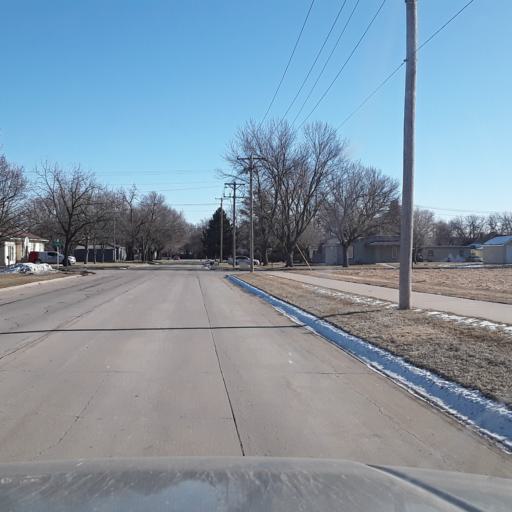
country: US
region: Nebraska
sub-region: Adams County
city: Hastings
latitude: 40.5784
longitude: -98.4056
